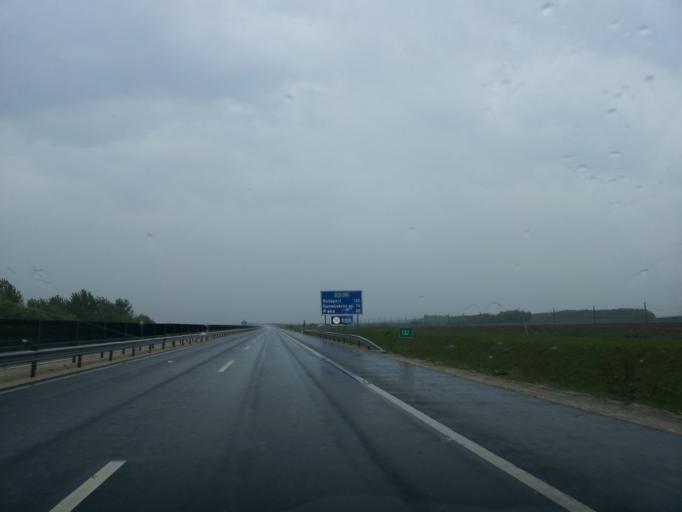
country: HU
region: Tolna
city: Tolna
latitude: 46.4184
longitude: 18.7299
